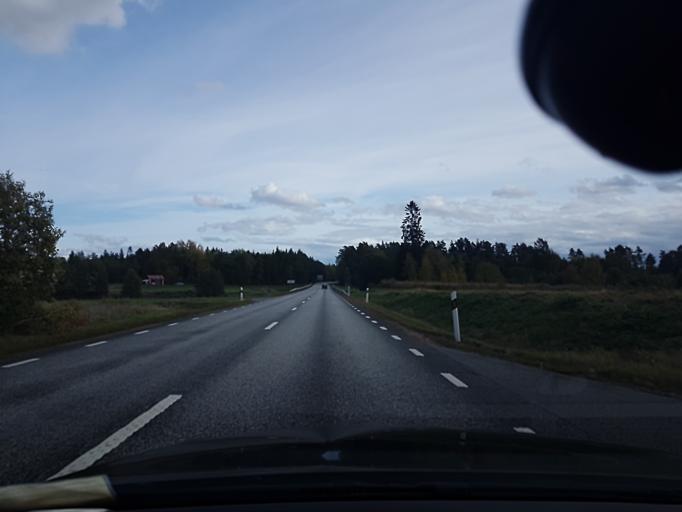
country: SE
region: Joenkoeping
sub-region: Varnamo Kommun
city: Bredaryd
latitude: 57.1795
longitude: 13.7526
